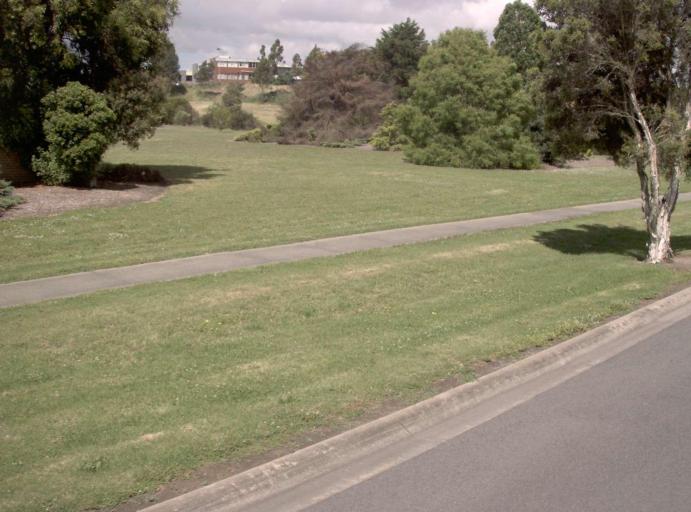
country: AU
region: Victoria
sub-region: Latrobe
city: Moe
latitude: -38.1818
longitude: 146.2749
